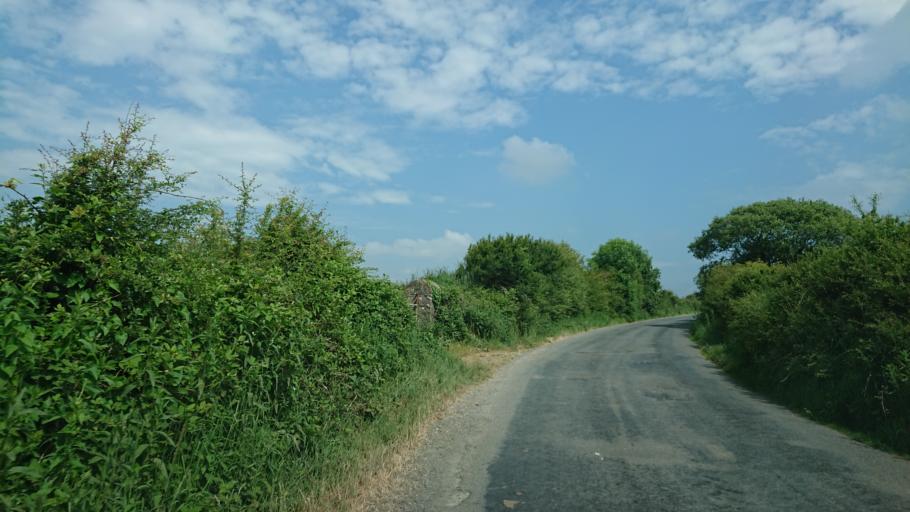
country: IE
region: Munster
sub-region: Waterford
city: Dunmore East
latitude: 52.2264
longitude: -7.0060
